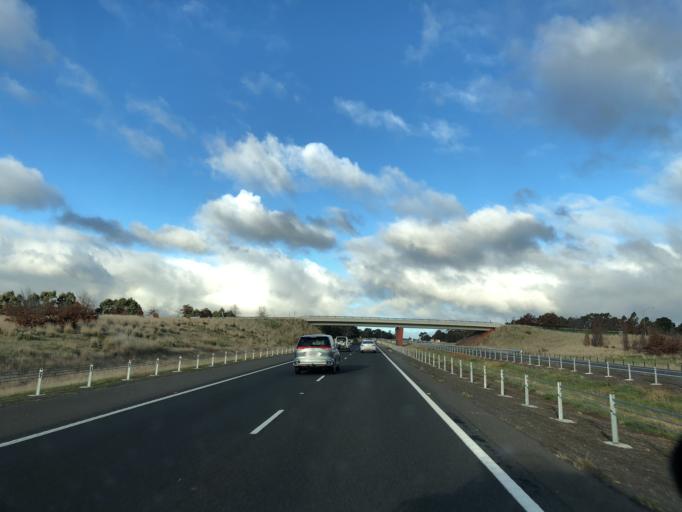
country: AU
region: Victoria
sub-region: Mount Alexander
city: Castlemaine
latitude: -37.2412
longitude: 144.4622
